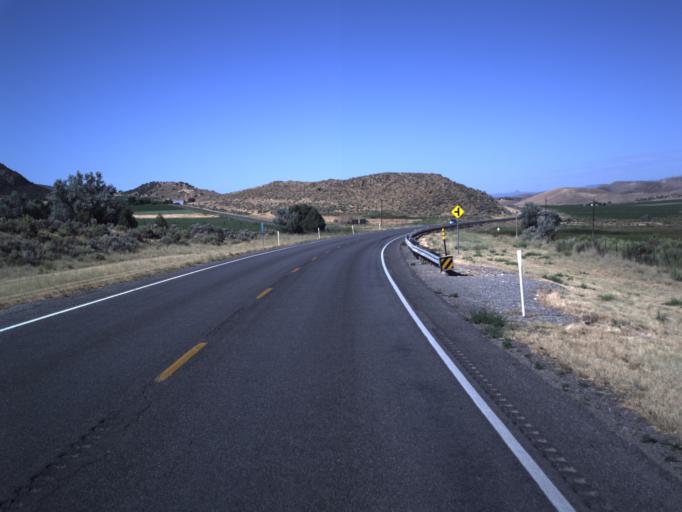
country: US
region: Utah
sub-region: Sanpete County
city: Manti
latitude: 39.2361
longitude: -111.6600
